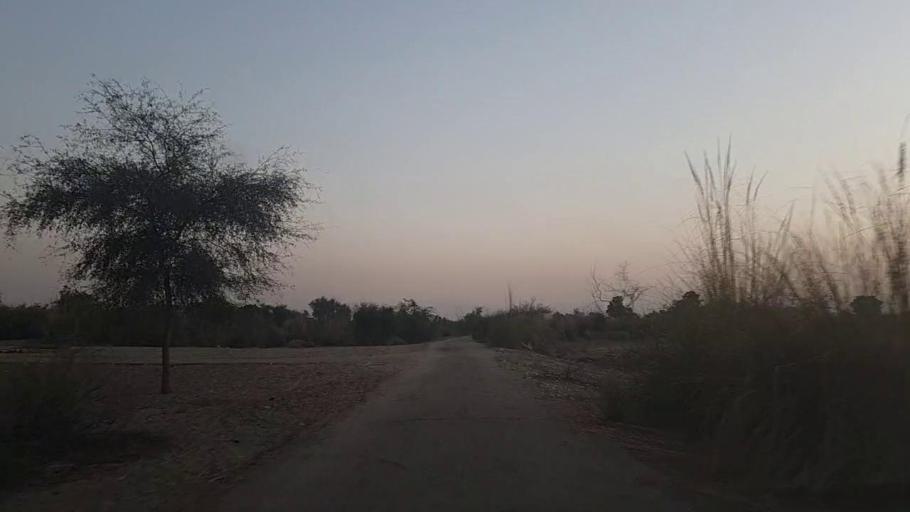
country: PK
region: Sindh
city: Jam Sahib
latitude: 26.3900
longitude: 68.8094
